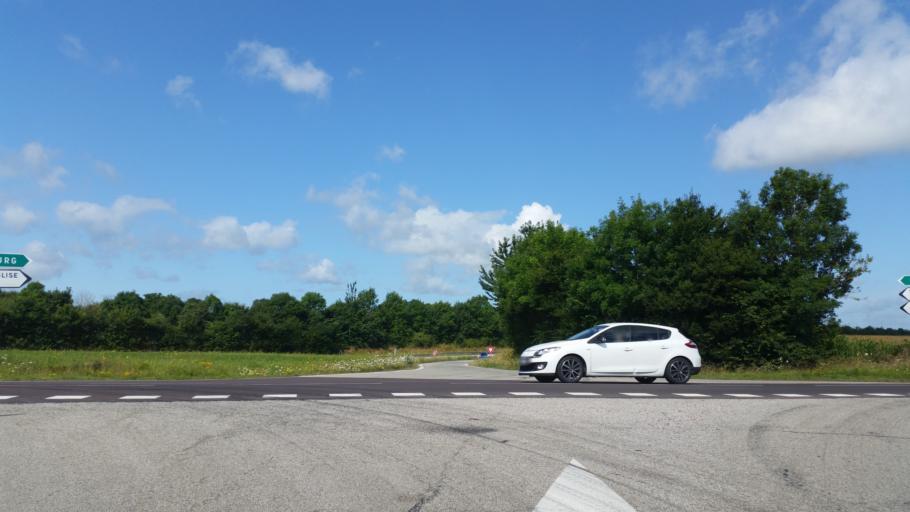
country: FR
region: Lower Normandy
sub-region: Departement de la Manche
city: Carentan
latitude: 49.3362
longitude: -1.2627
